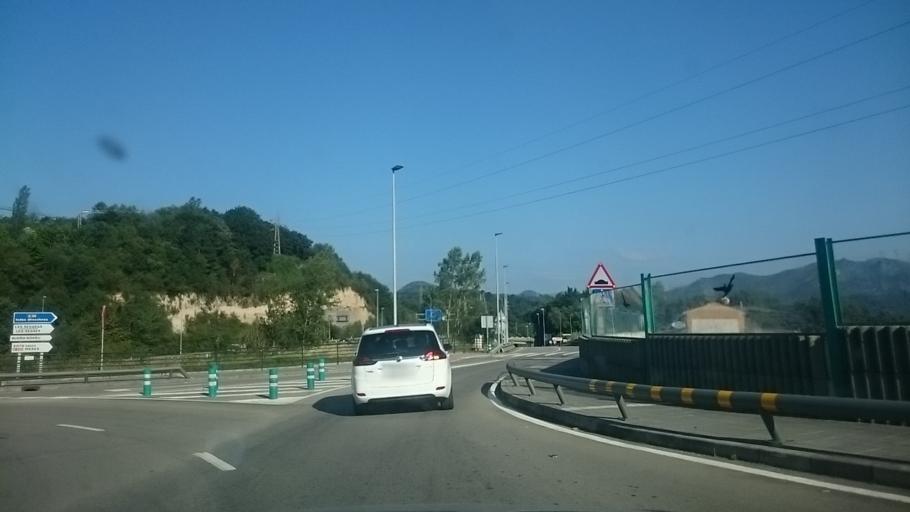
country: ES
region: Asturias
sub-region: Province of Asturias
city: Oviedo
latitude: 43.3256
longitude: -5.8773
